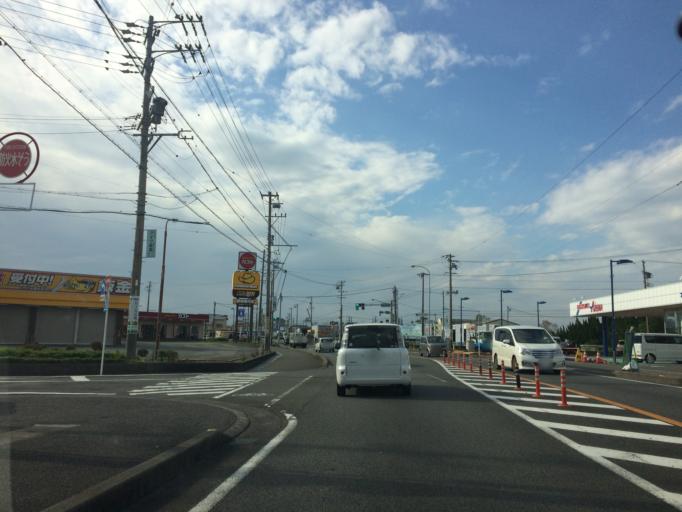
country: JP
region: Shizuoka
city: Shimada
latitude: 34.7698
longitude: 138.2503
